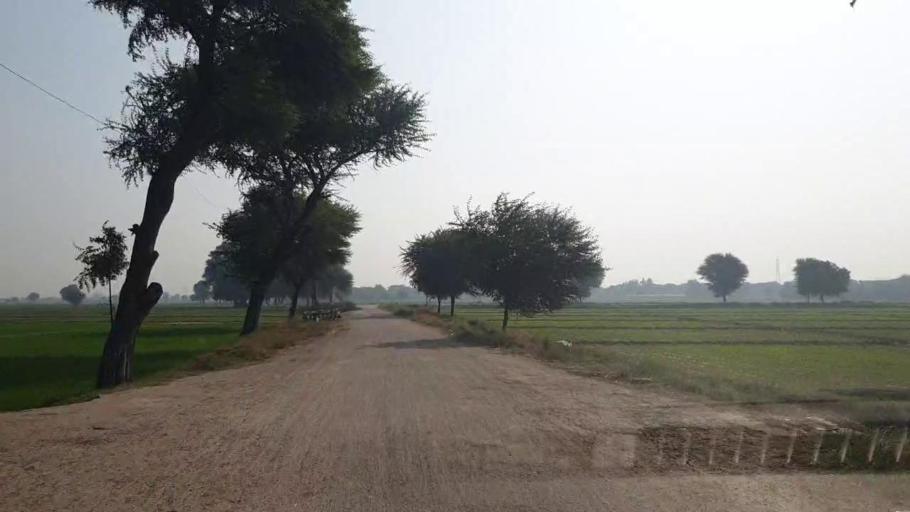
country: PK
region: Sindh
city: Kotri
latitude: 25.3551
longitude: 68.3090
